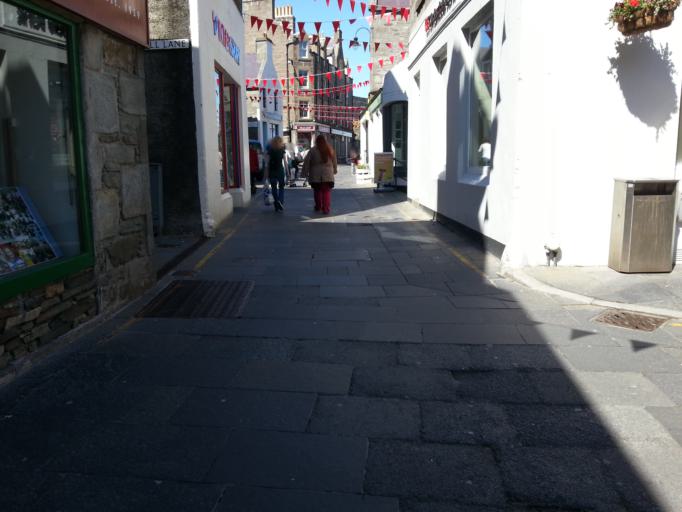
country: GB
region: Scotland
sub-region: Shetland Islands
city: Shetland
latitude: 60.1543
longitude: -1.1436
